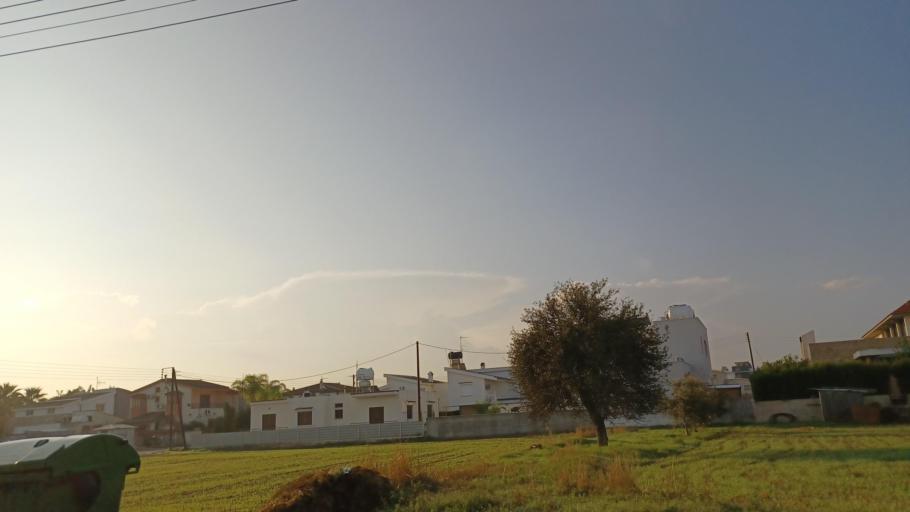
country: CY
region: Lefkosia
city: Lympia
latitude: 34.9948
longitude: 33.4686
